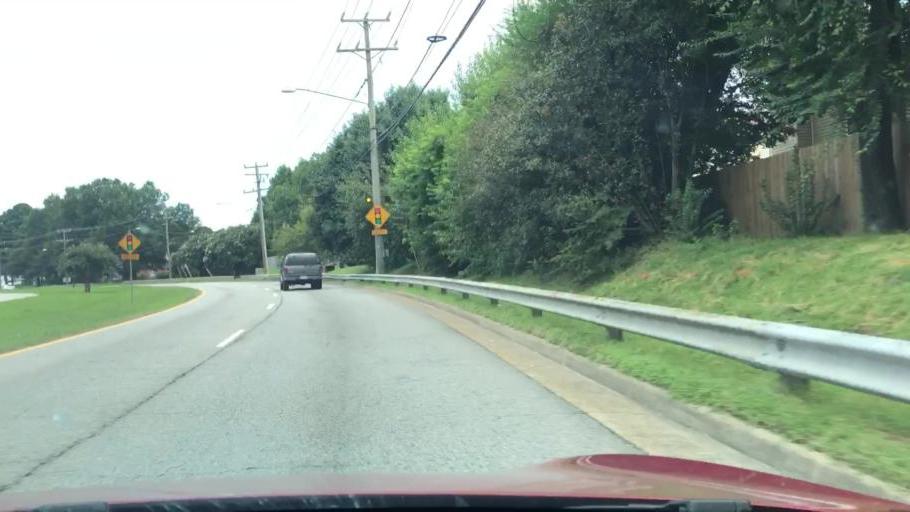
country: US
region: Virginia
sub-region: City of Chesapeake
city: Chesapeake
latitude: 36.8815
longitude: -76.1331
